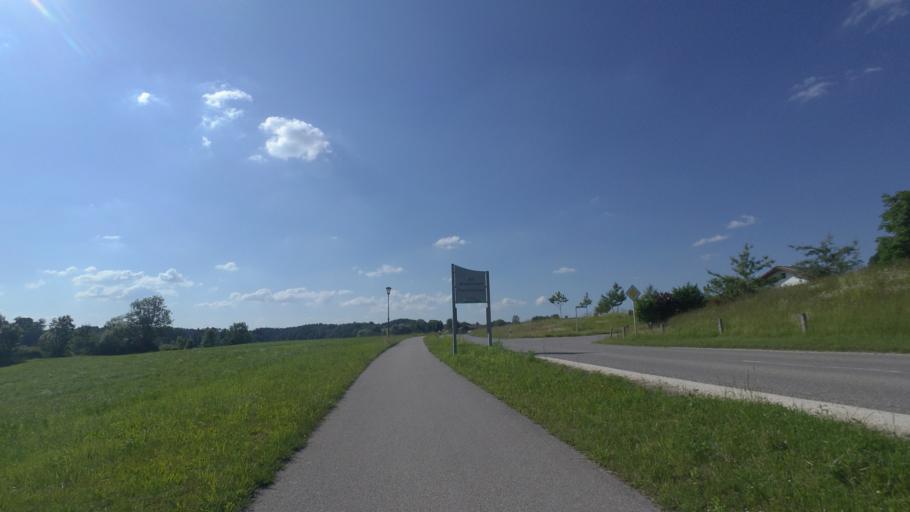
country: DE
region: Bavaria
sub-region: Upper Bavaria
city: Seeon-Seebruck
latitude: 47.9627
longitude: 12.4980
